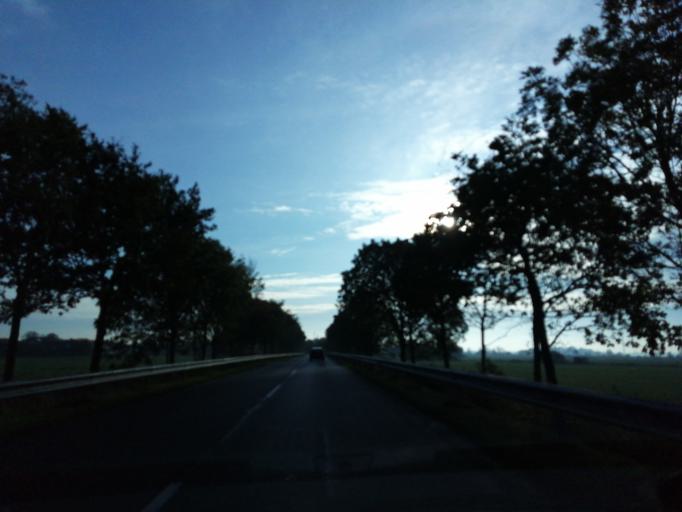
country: DE
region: Lower Saxony
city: Sillenstede
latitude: 53.6231
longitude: 8.0192
